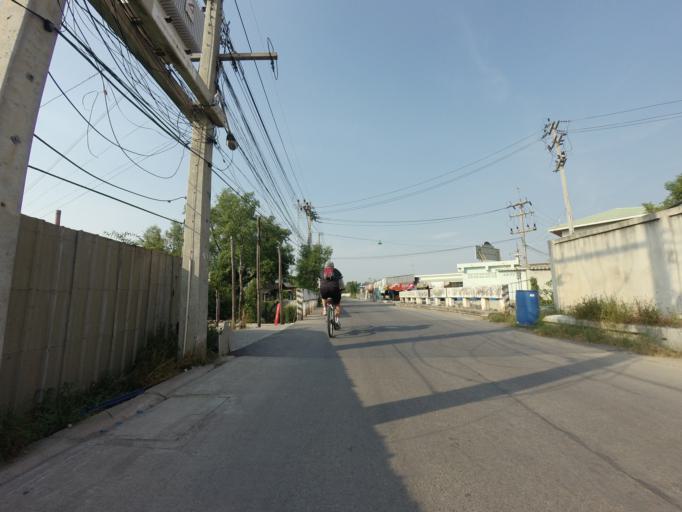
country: TH
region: Samut Sakhon
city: Samut Sakhon
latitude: 13.5149
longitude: 100.2792
